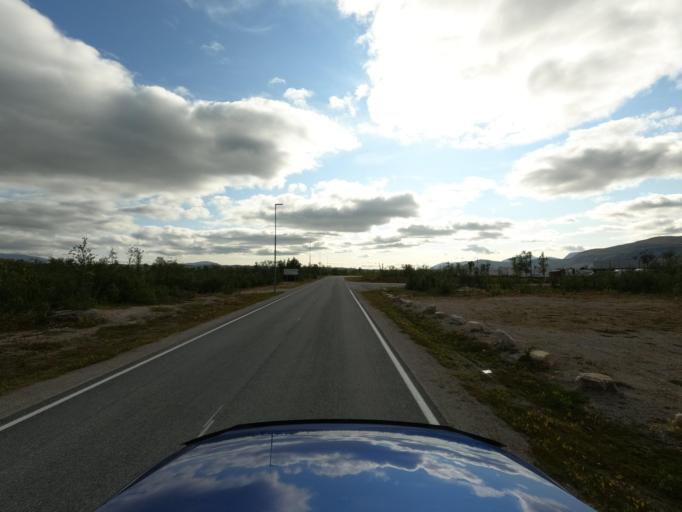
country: NO
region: Finnmark Fylke
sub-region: Porsanger
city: Lakselv
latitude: 70.0646
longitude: 24.9847
